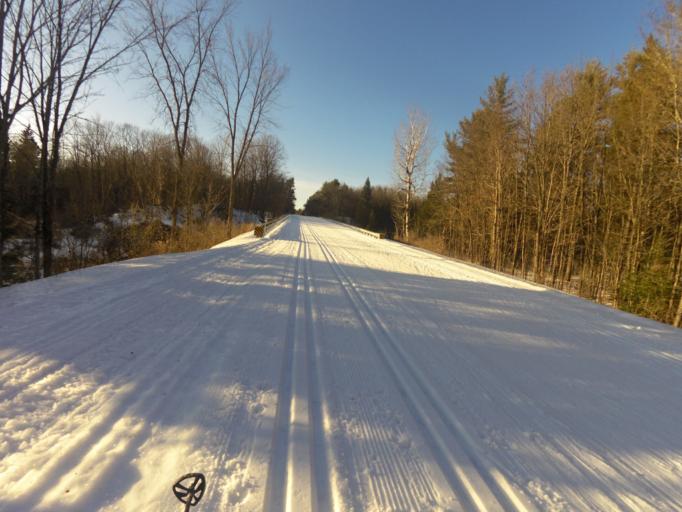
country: CA
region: Quebec
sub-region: Outaouais
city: Gatineau
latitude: 45.5207
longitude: -75.8311
